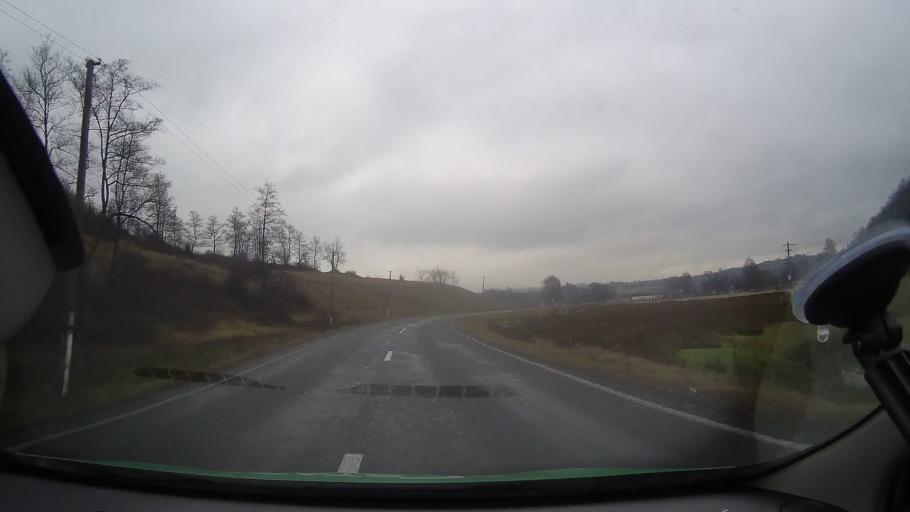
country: RO
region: Arad
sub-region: Comuna Varfurile
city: Varfurile
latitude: 46.3232
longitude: 22.4751
